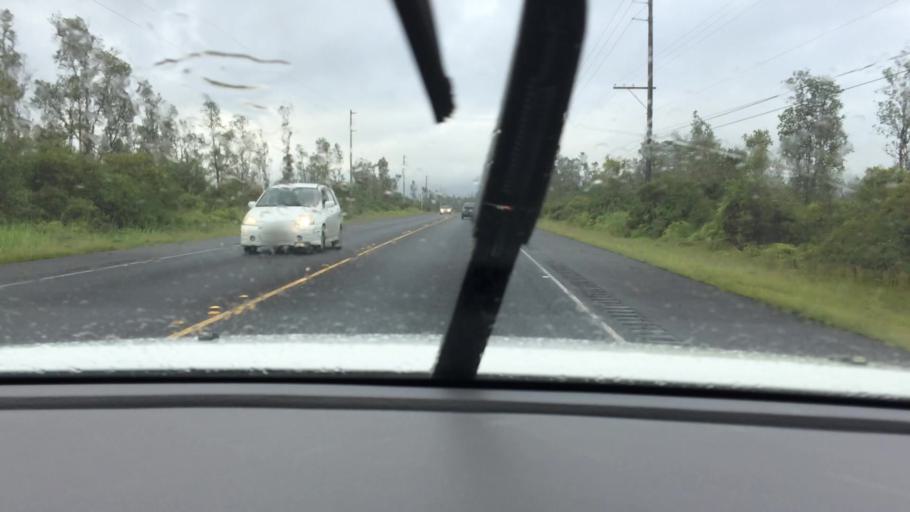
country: US
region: Hawaii
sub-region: Hawaii County
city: Hawaiian Paradise Park
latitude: 19.5173
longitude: -154.9653
